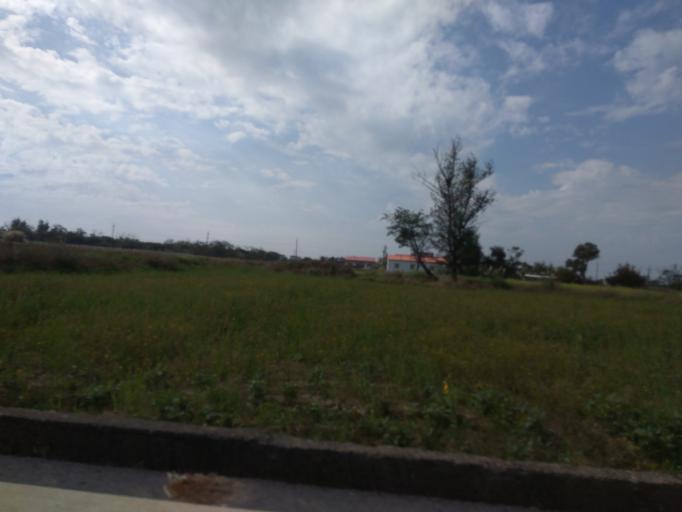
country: TW
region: Taiwan
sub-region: Hsinchu
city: Zhubei
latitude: 24.9551
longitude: 121.0079
